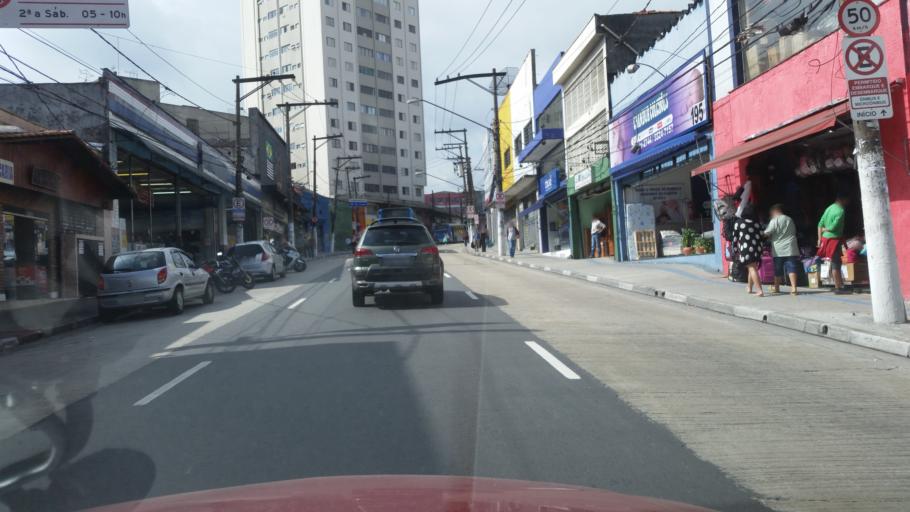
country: BR
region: Sao Paulo
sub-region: Diadema
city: Diadema
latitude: -23.6556
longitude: -46.7066
